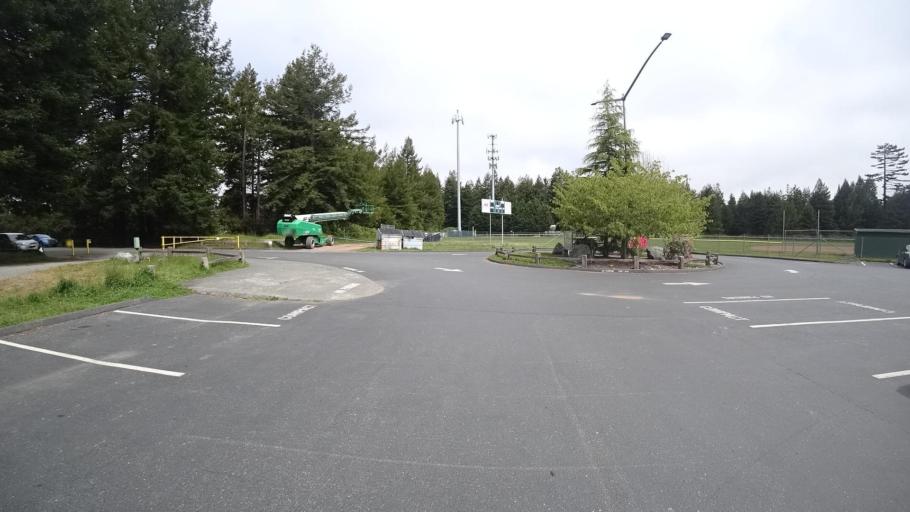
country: US
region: California
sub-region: Humboldt County
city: Cutten
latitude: 40.7697
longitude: -124.1390
